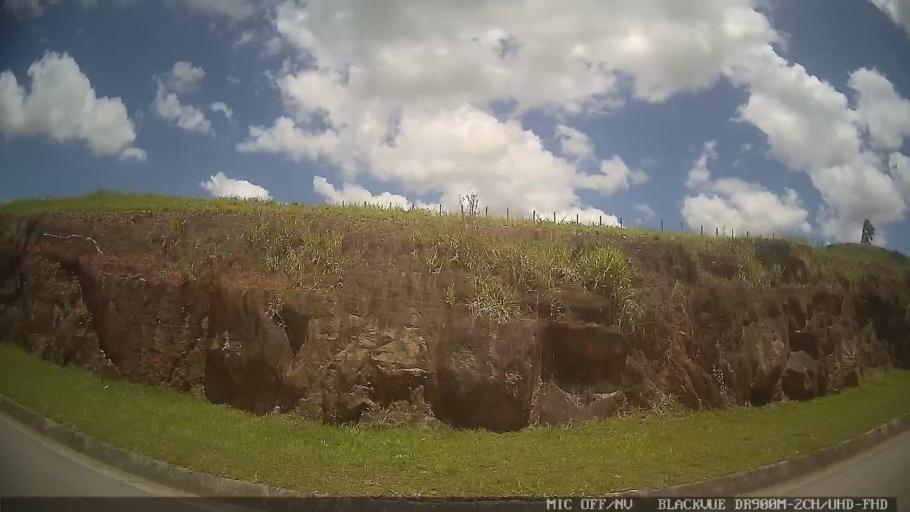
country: BR
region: Sao Paulo
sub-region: Santa Branca
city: Santa Branca
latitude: -23.4100
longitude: -45.6444
